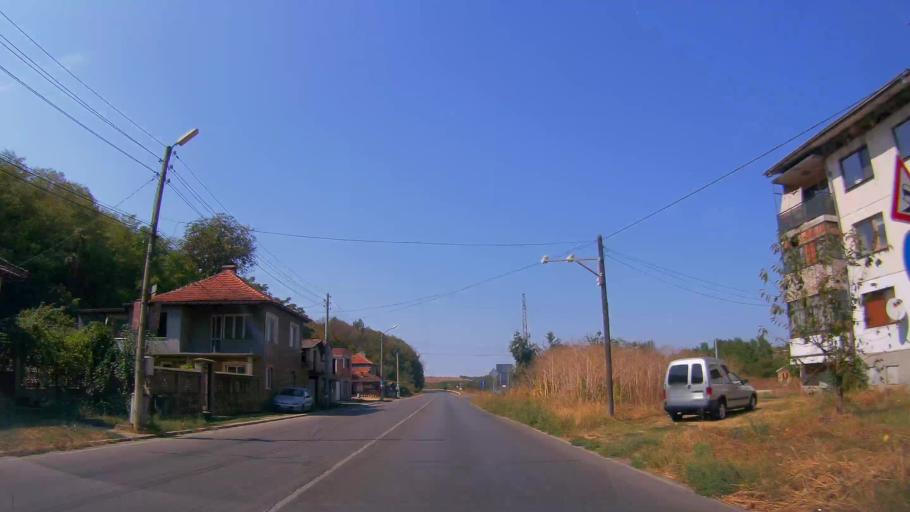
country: BG
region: Razgrad
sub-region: Obshtina Tsar Kaloyan
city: Tsar Kaloyan
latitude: 43.6121
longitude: 26.2306
